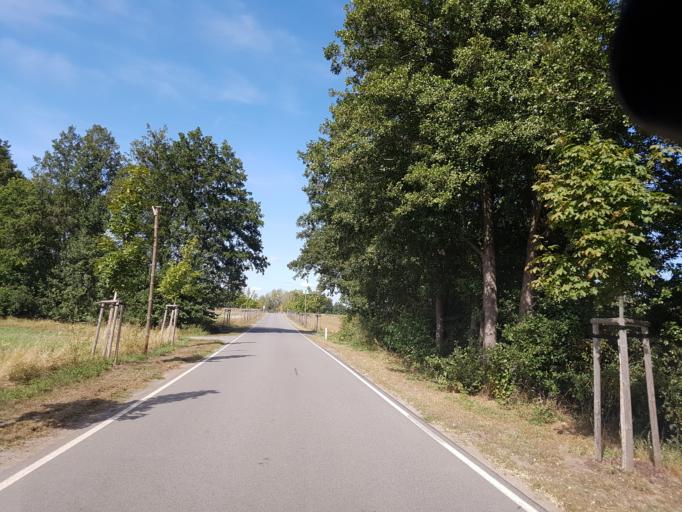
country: DE
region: Brandenburg
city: Luckau
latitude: 51.8547
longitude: 13.6328
